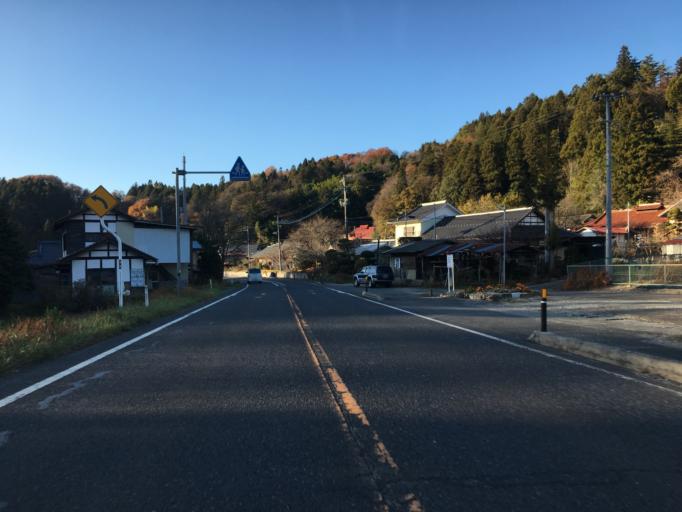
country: JP
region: Fukushima
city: Sukagawa
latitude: 37.3014
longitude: 140.5096
